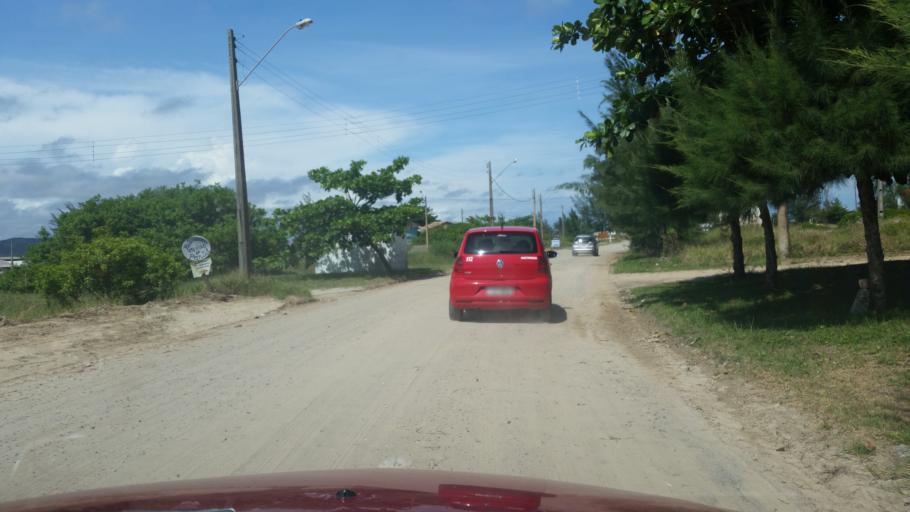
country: BR
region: Sao Paulo
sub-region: Iguape
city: Iguape
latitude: -24.7001
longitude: -47.4607
